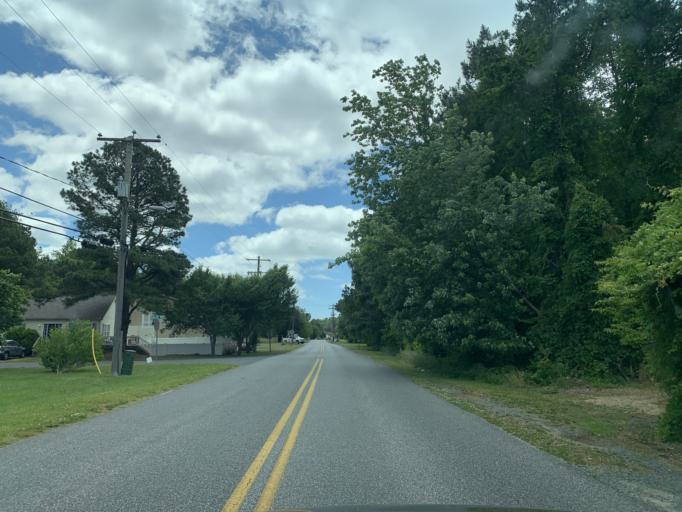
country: US
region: Maryland
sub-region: Worcester County
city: West Ocean City
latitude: 38.3510
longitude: -75.1173
